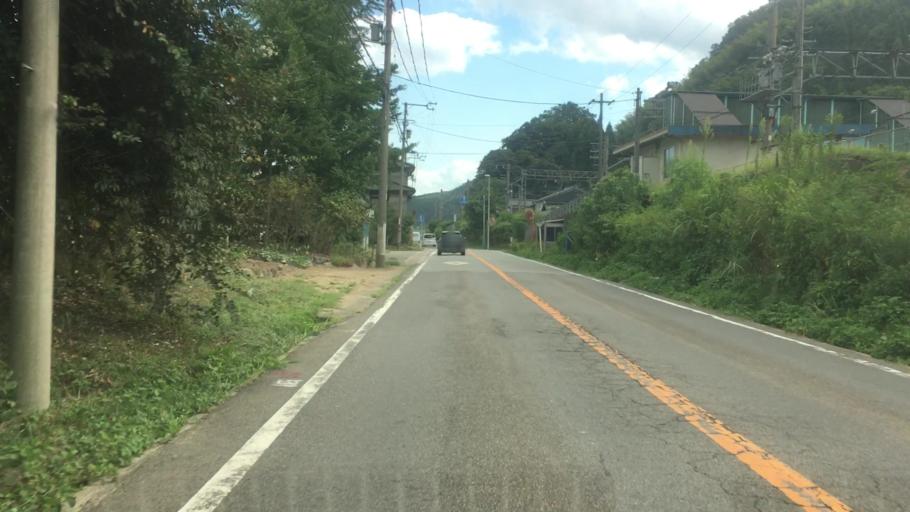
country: JP
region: Hyogo
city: Toyooka
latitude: 35.5890
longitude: 134.7994
